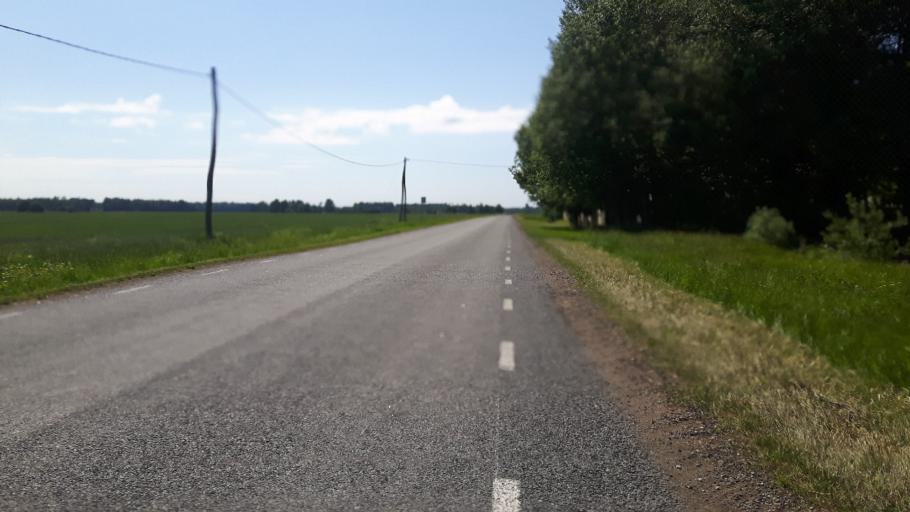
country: EE
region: Paernumaa
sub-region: Vaendra vald (alev)
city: Vandra
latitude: 58.6212
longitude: 25.0211
